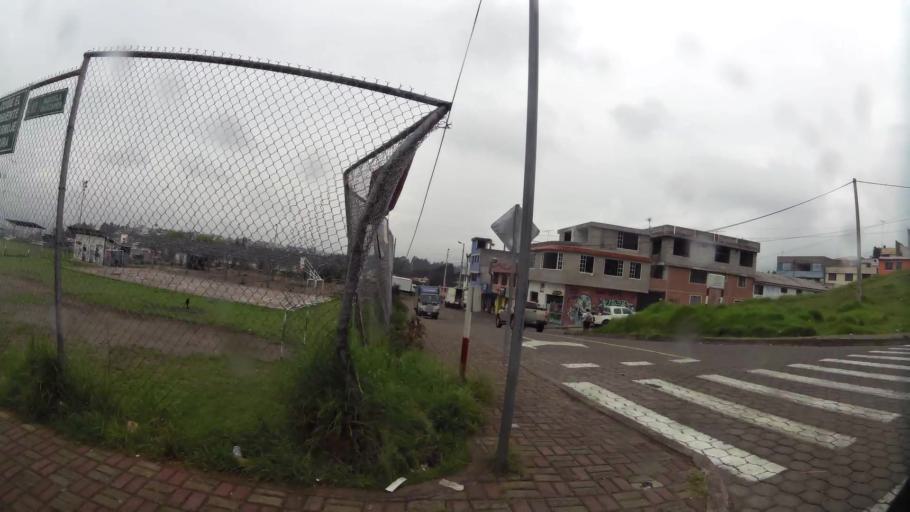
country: EC
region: Pichincha
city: Sangolqui
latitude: -0.2787
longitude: -78.4737
